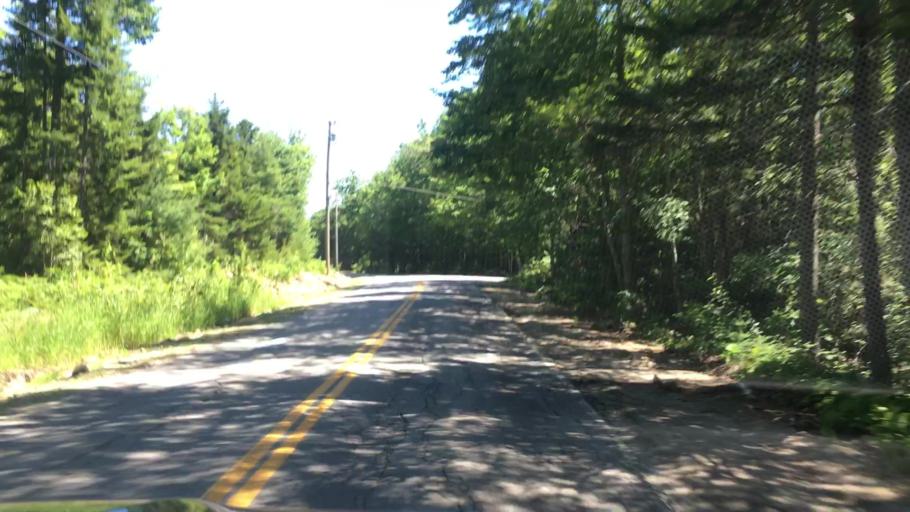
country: US
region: Maine
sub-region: Hancock County
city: Penobscot
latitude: 44.4395
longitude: -68.7084
